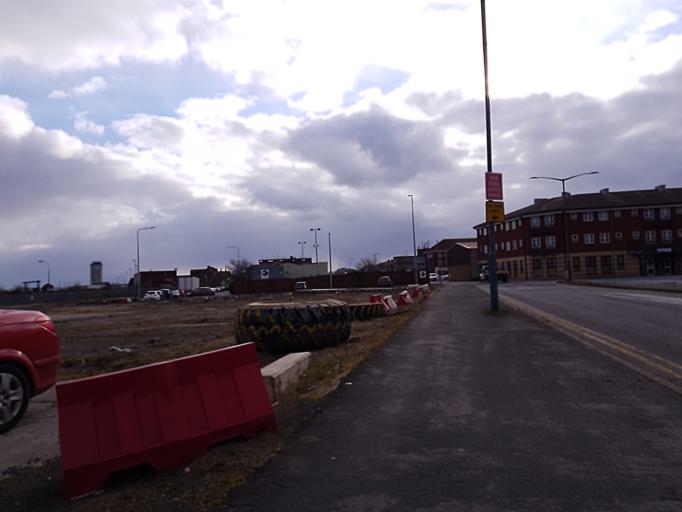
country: GB
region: England
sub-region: North East Lincolnshire
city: Grimsby
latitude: 53.5762
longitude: -0.0730
